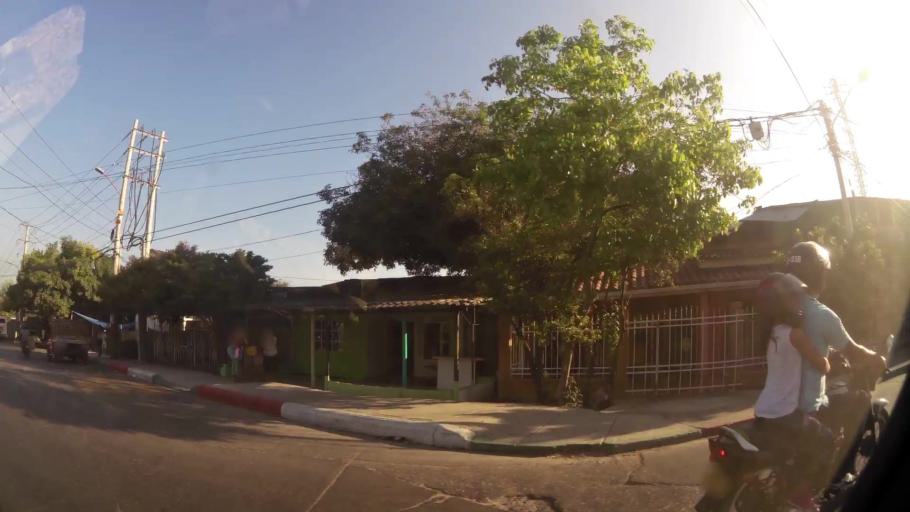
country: CO
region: Bolivar
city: Cartagena
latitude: 10.4038
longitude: -75.5060
